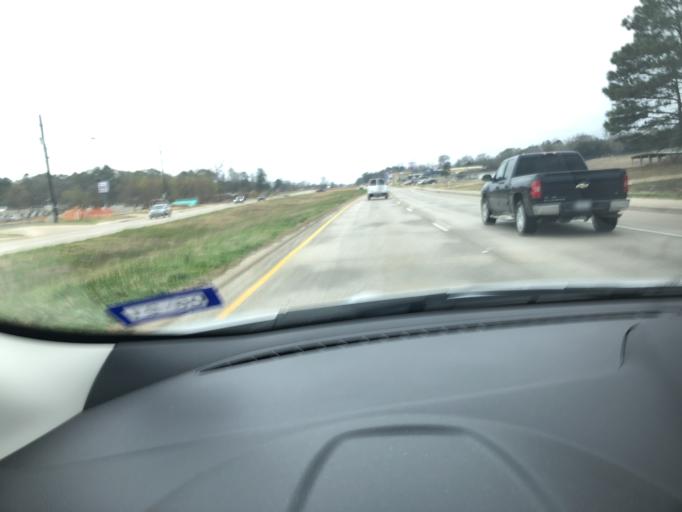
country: US
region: Texas
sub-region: Nacogdoches County
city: Nacogdoches
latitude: 31.5658
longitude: -94.6780
